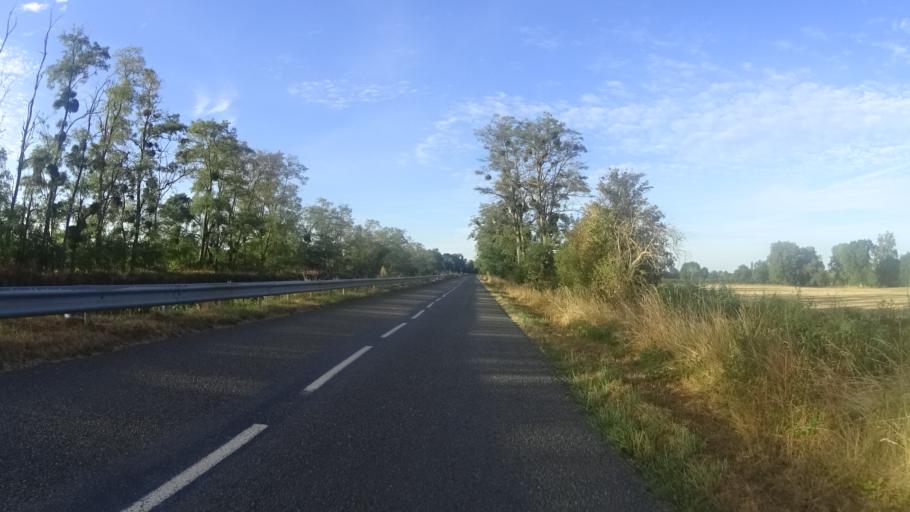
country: FR
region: Bourgogne
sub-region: Departement de Saone-et-Loire
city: Palinges
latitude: 46.4969
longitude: 4.1834
